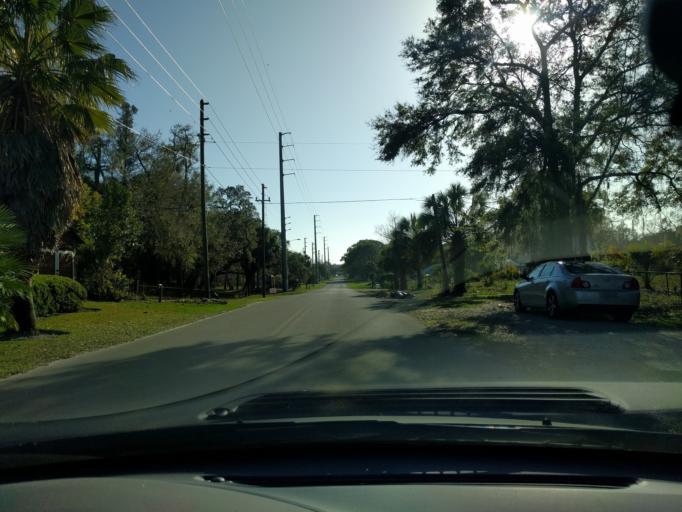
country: US
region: Florida
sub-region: Franklin County
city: Apalachicola
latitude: 29.7264
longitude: -84.9878
